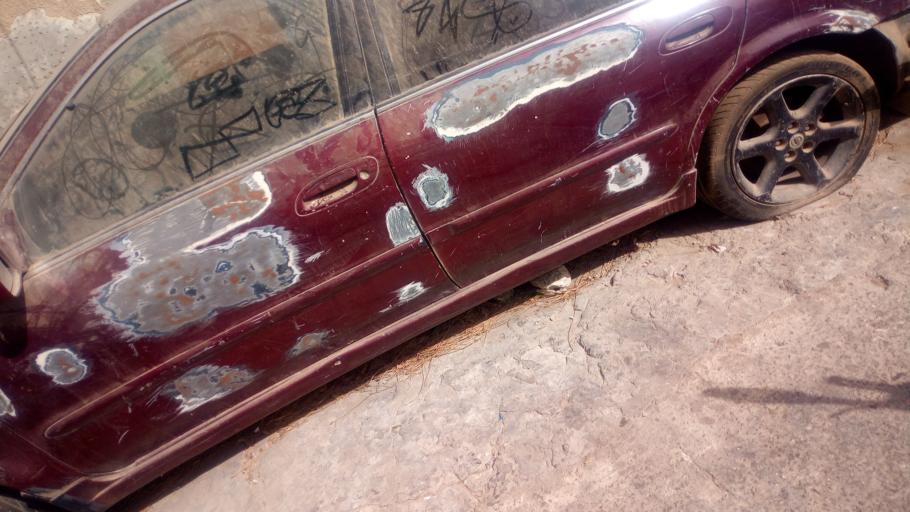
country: SN
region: Dakar
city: Dakar
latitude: 14.6913
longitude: -17.4489
